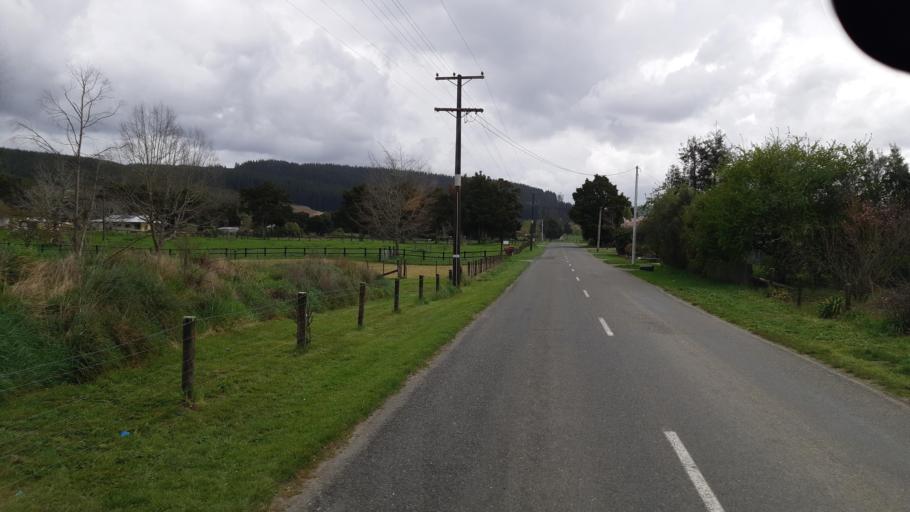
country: NZ
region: Tasman
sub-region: Tasman District
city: Wakefield
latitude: -41.4003
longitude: 173.0350
